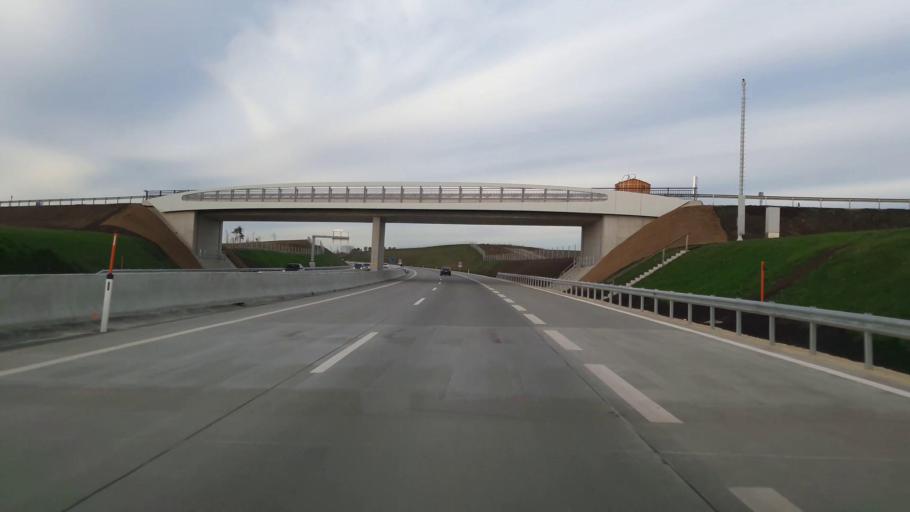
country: AT
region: Lower Austria
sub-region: Politischer Bezirk Mistelbach
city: Herrnbaumgarten
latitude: 48.6532
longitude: 16.6908
